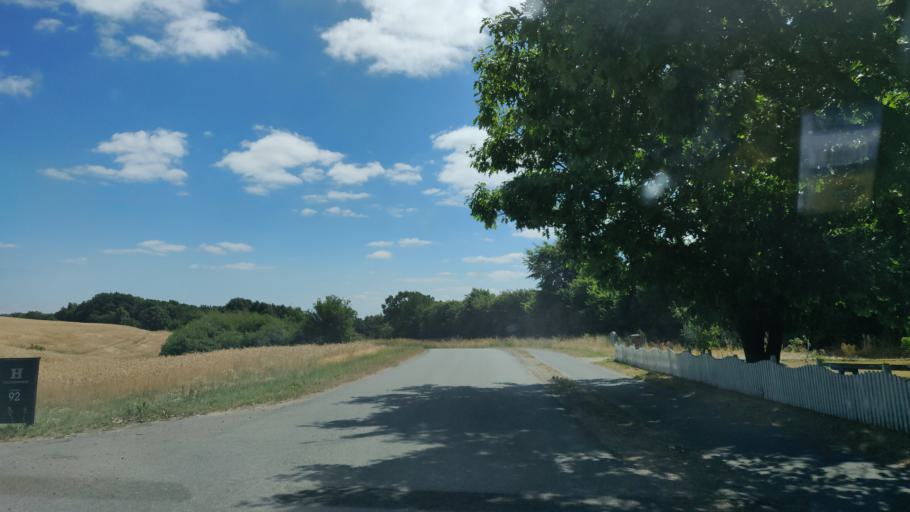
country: DK
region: South Denmark
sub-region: Kolding Kommune
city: Kolding
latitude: 55.5394
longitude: 9.5184
